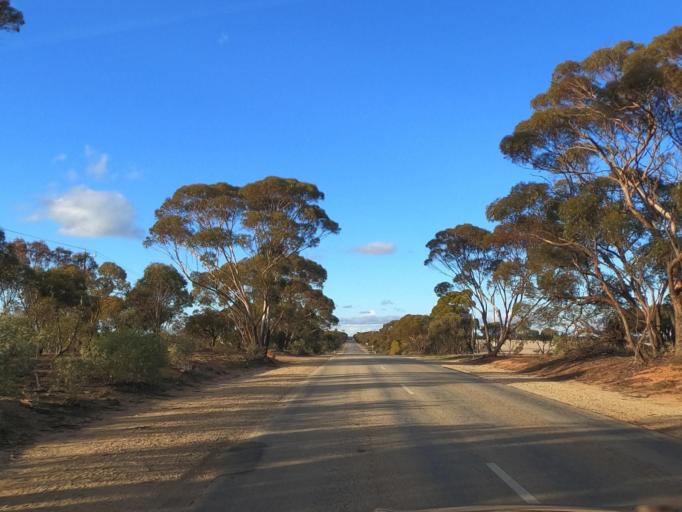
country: AU
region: Victoria
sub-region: Swan Hill
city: Swan Hill
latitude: -35.3490
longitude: 143.5138
